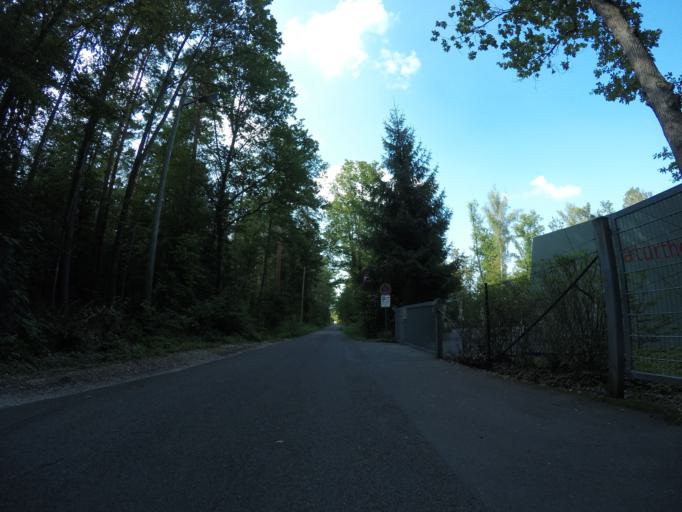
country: DE
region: Baden-Wuerttemberg
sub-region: Tuebingen Region
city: Reutlingen
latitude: 48.4701
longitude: 9.1865
